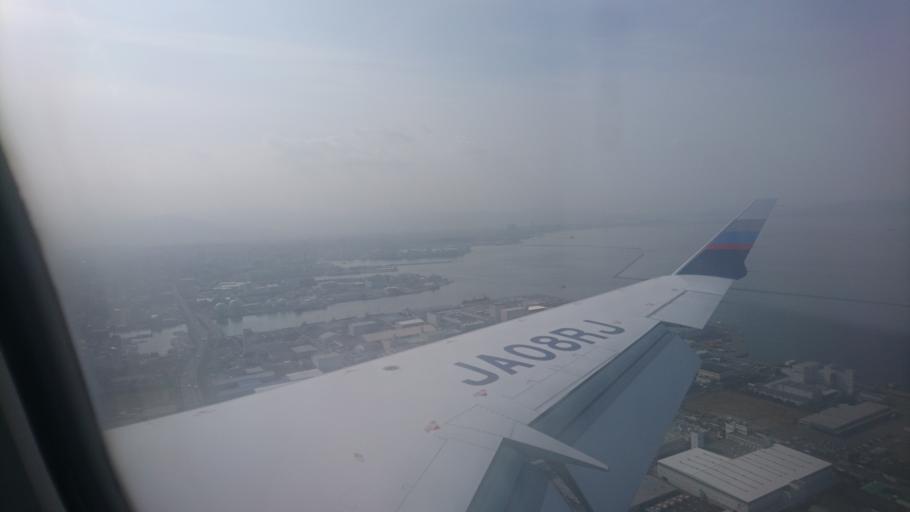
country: JP
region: Fukuoka
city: Fukuoka-shi
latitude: 33.6320
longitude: 130.4188
